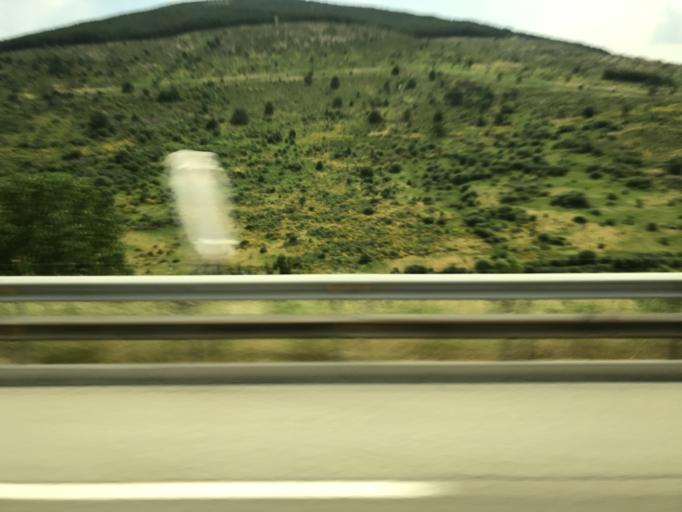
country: ES
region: Madrid
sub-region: Provincia de Madrid
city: Robregordo
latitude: 41.1105
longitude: -3.5884
